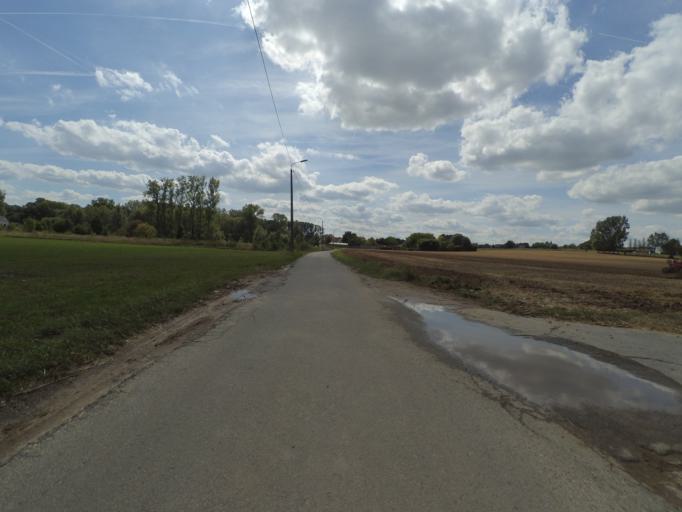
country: BE
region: Flanders
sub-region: Provincie Oost-Vlaanderen
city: Zottegem
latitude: 50.8538
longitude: 3.7634
